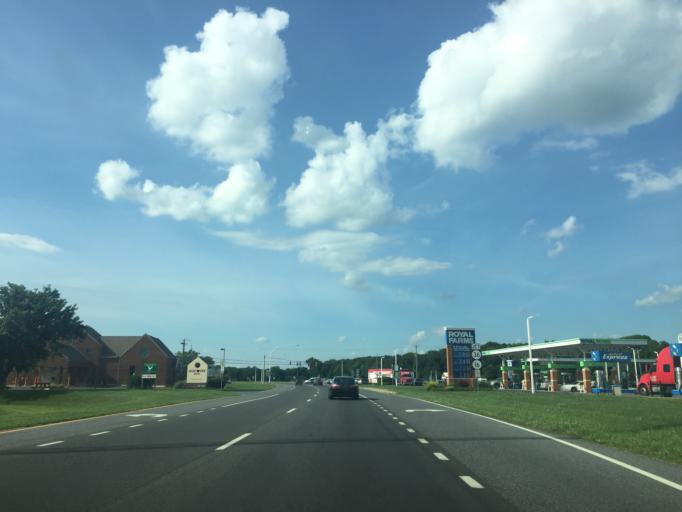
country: US
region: Delaware
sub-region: Sussex County
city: Bridgeville
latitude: 38.8045
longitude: -75.5843
